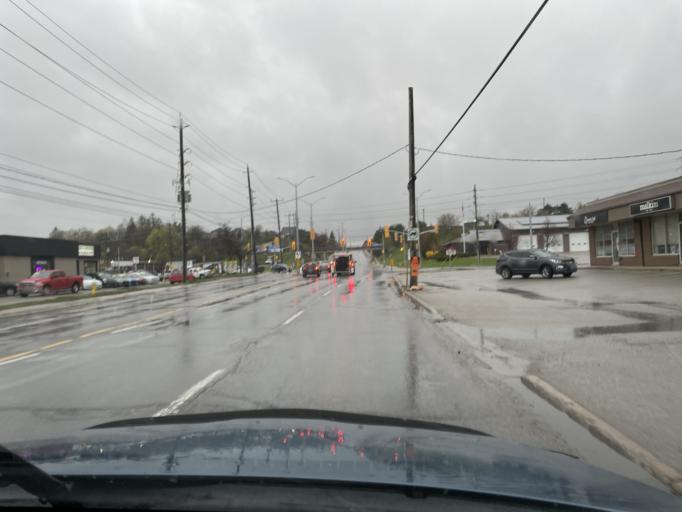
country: CA
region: Ontario
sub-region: Wellington County
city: Guelph
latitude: 43.5549
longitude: -80.2279
